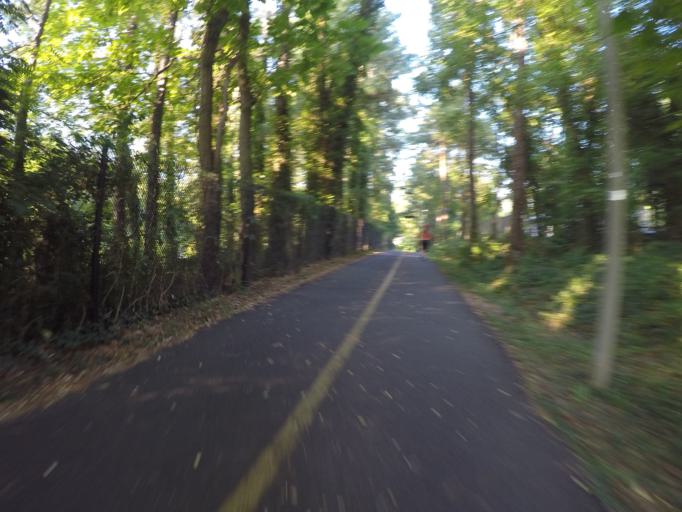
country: US
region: Virginia
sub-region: Arlington County
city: Arlington
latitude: 38.8919
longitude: -77.1025
